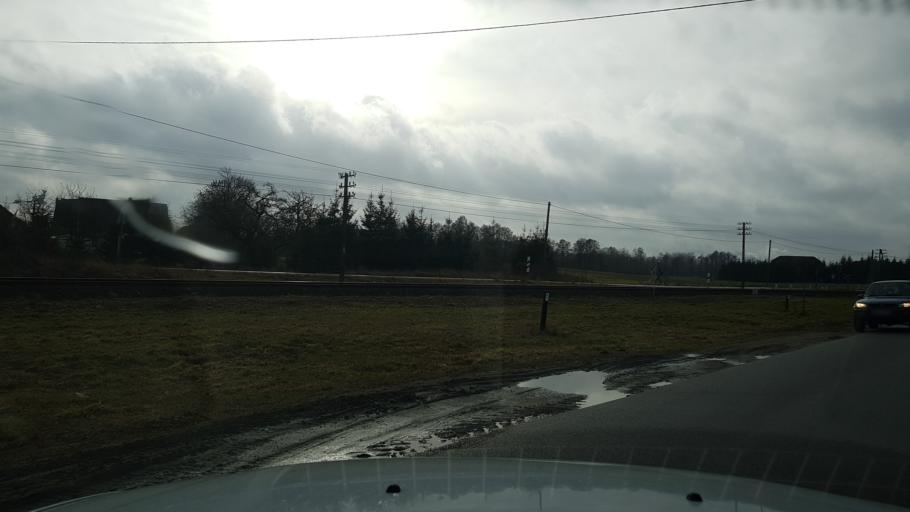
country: PL
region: West Pomeranian Voivodeship
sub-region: Powiat szczecinecki
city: Szczecinek
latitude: 53.7101
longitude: 16.7437
